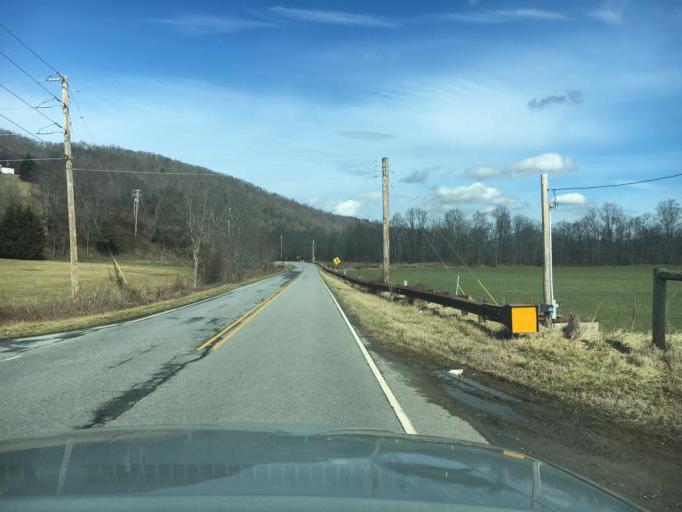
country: US
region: North Carolina
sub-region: Haywood County
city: Clyde
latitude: 35.4904
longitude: -82.8854
